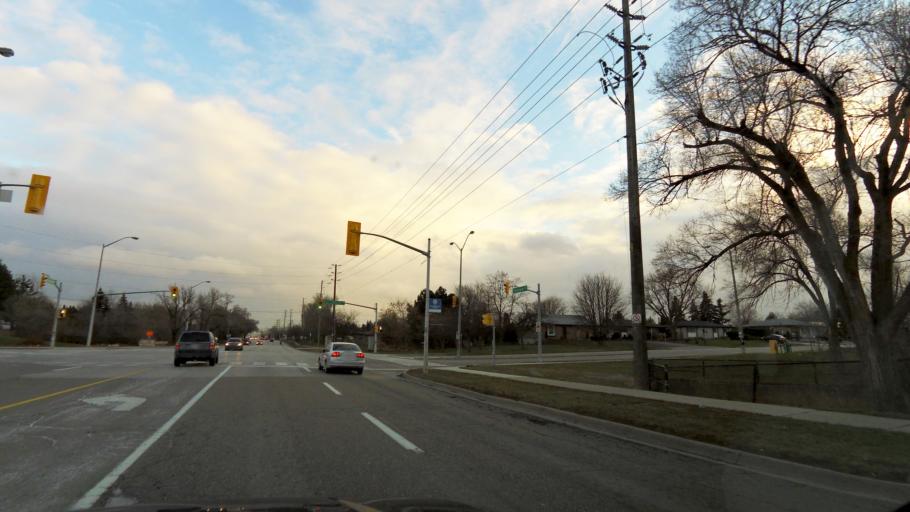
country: CA
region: Ontario
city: Brampton
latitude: 43.7200
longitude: -79.6879
